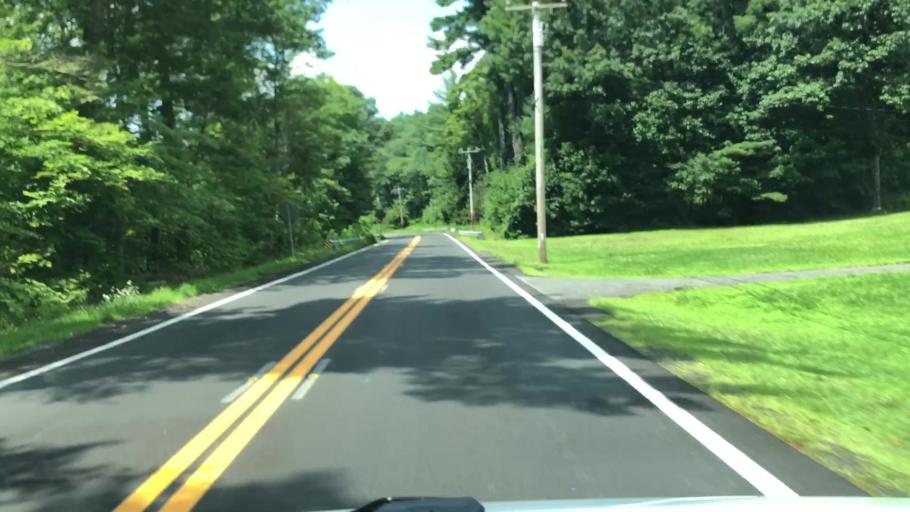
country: US
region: Massachusetts
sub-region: Franklin County
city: Ashfield
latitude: 42.5177
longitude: -72.7480
